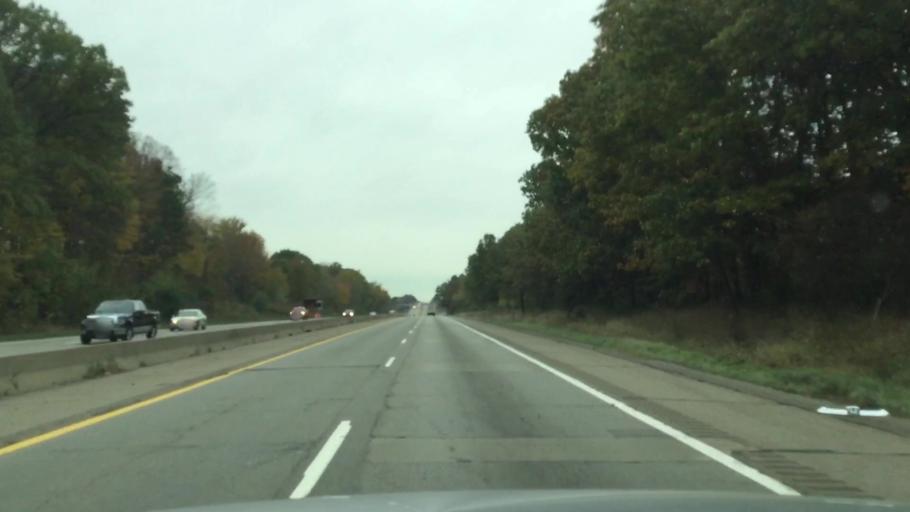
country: US
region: Michigan
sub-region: Jackson County
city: Spring Arbor
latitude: 42.2691
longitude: -84.5235
